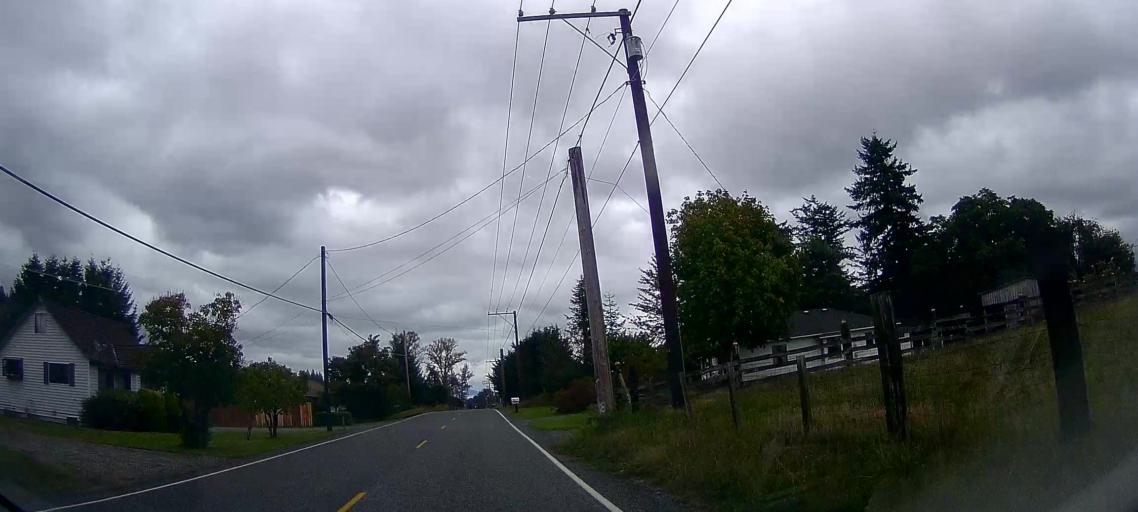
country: US
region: Washington
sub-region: Skagit County
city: Sedro-Woolley
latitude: 48.5270
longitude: -122.0780
